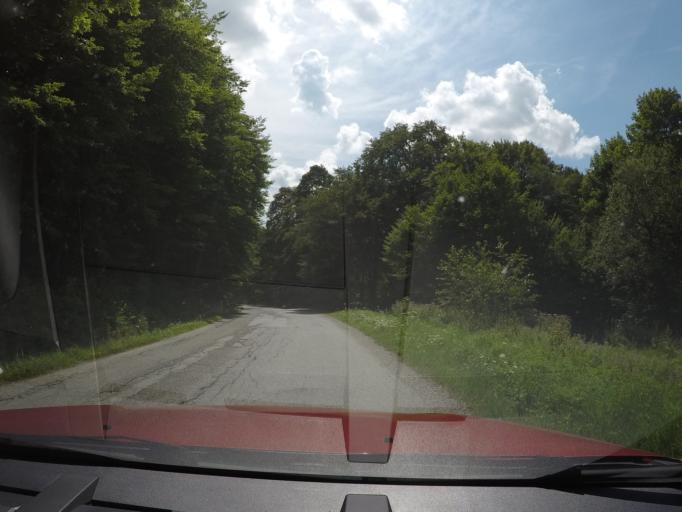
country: SK
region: Kosicky
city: Gelnica
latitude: 48.9129
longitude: 21.0305
